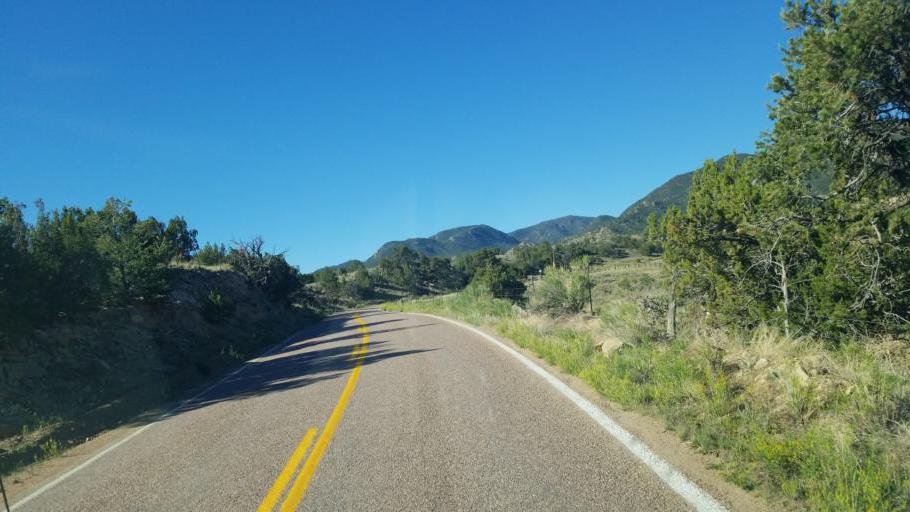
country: US
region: Colorado
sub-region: Fremont County
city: Canon City
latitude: 38.4449
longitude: -105.3736
